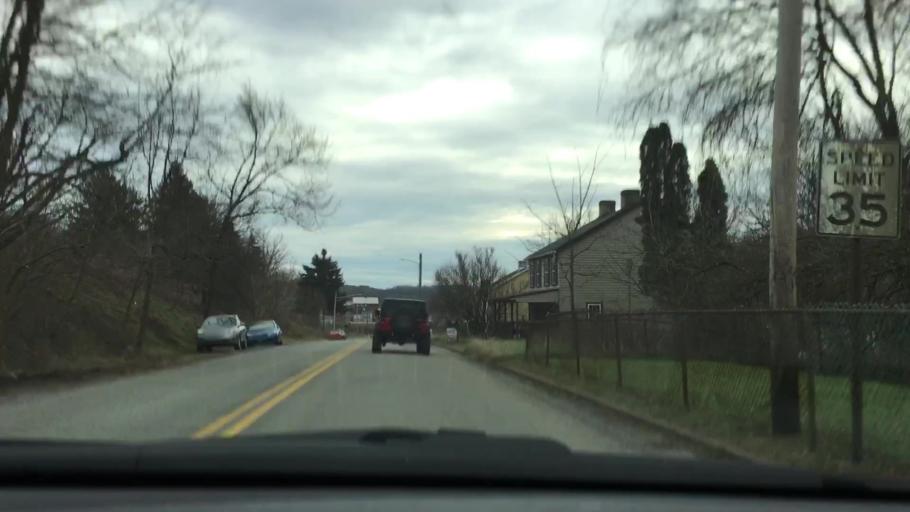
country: US
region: Pennsylvania
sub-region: Washington County
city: Midland
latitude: 40.2601
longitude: -80.2193
